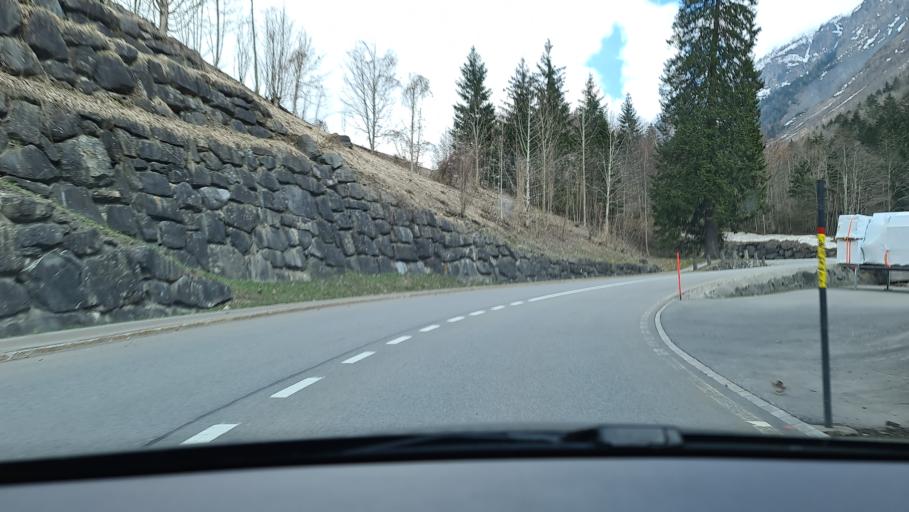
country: CH
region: Uri
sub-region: Uri
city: Burglen
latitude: 46.8706
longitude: 8.7317
